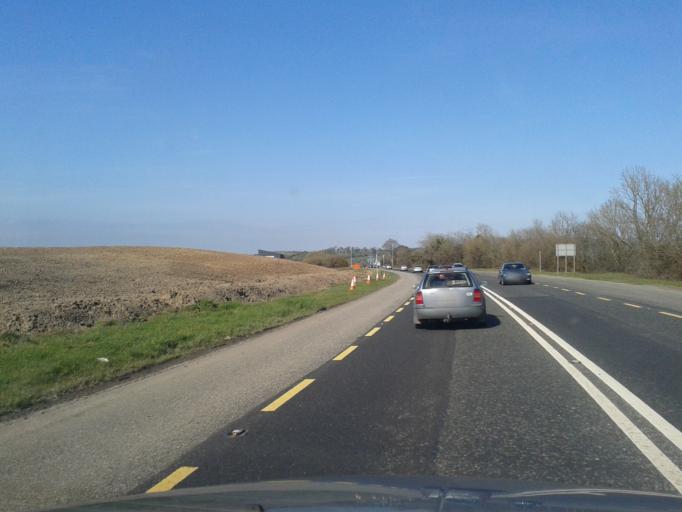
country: IE
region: Leinster
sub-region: Wicklow
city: Arklow
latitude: 52.8776
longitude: -6.1008
